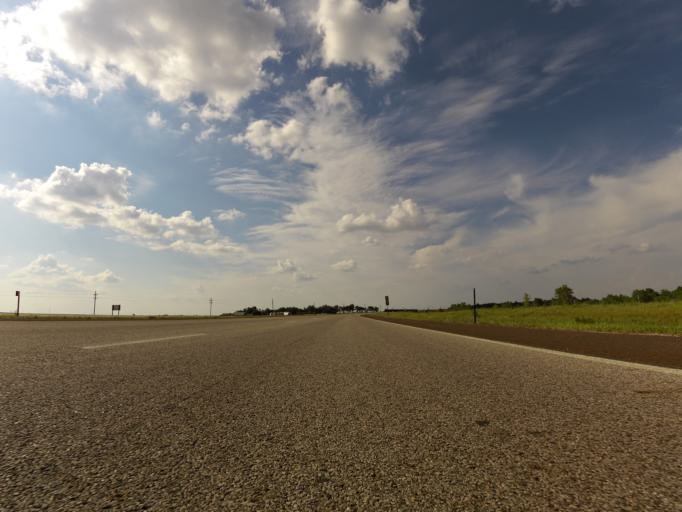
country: US
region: Kansas
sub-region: Reno County
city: South Hutchinson
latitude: 37.9748
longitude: -97.9388
